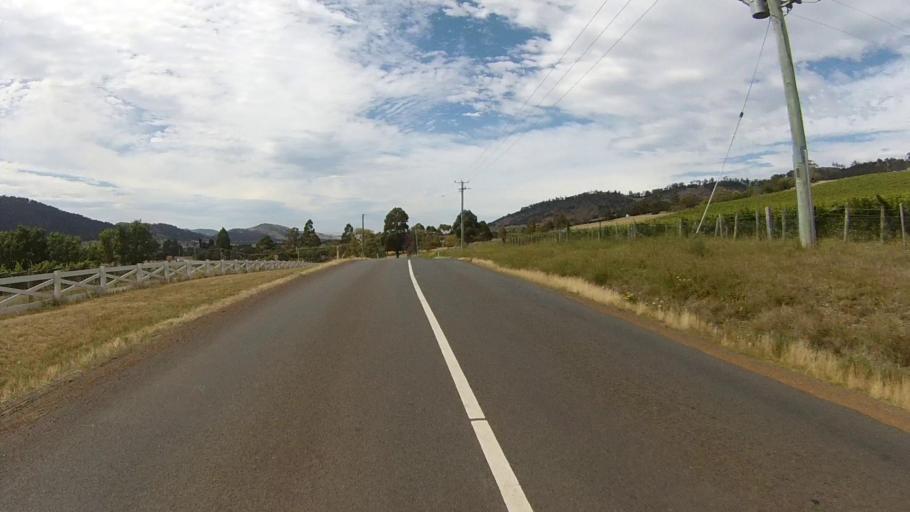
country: AU
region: Tasmania
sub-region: Brighton
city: Old Beach
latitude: -42.7077
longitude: 147.3692
